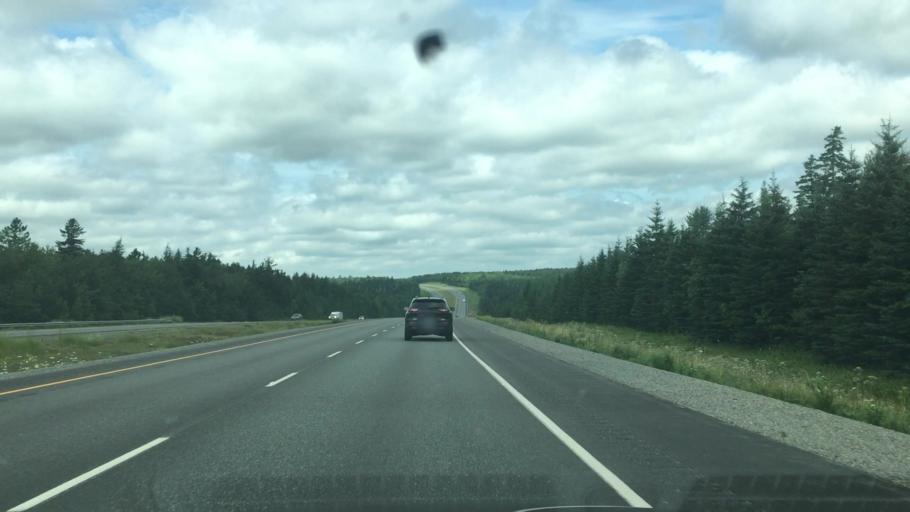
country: CA
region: Nova Scotia
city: Springhill
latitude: 45.7255
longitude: -64.0579
